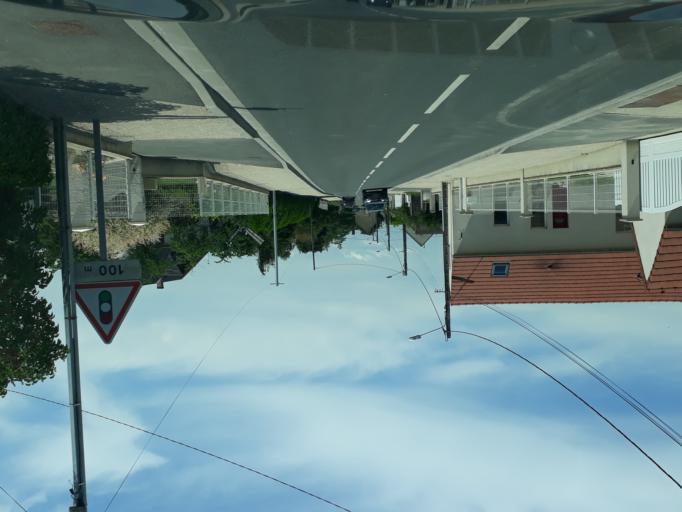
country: FR
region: Centre
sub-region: Departement du Loiret
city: Sandillon
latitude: 47.8448
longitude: 2.0245
